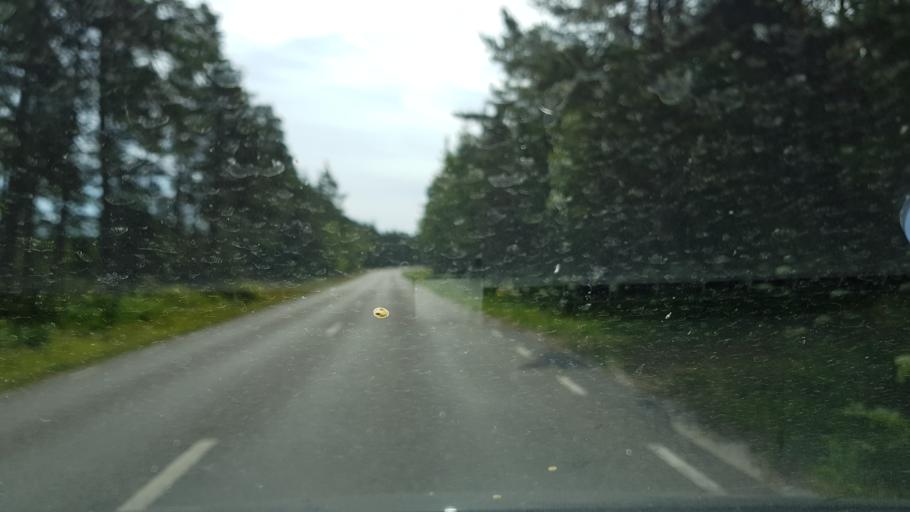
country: SE
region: Gotland
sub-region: Gotland
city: Hemse
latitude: 57.4696
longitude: 18.5576
